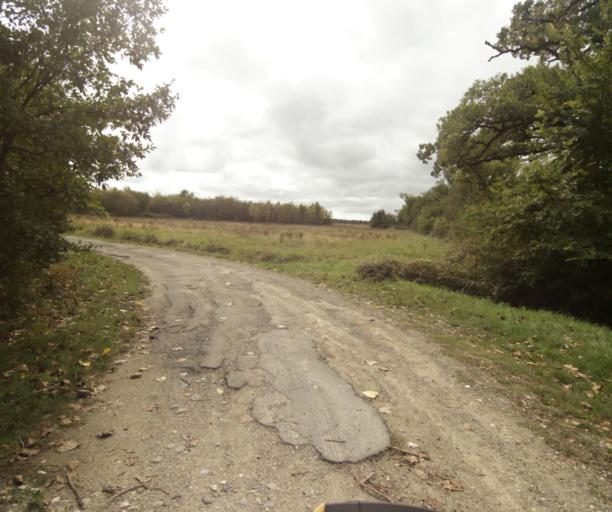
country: FR
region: Midi-Pyrenees
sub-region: Departement du Tarn-et-Garonne
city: Montech
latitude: 43.9775
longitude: 1.2499
